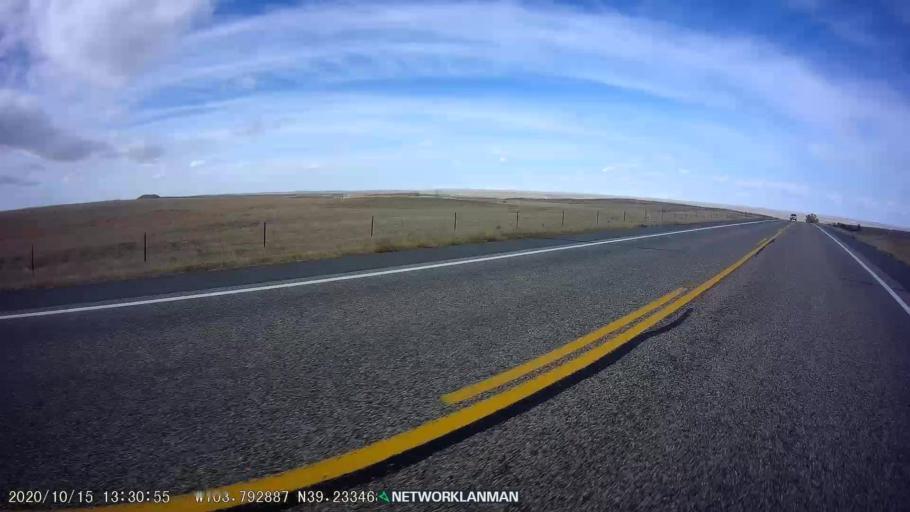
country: US
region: Colorado
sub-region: Lincoln County
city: Limon
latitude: 39.2339
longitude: -103.7923
